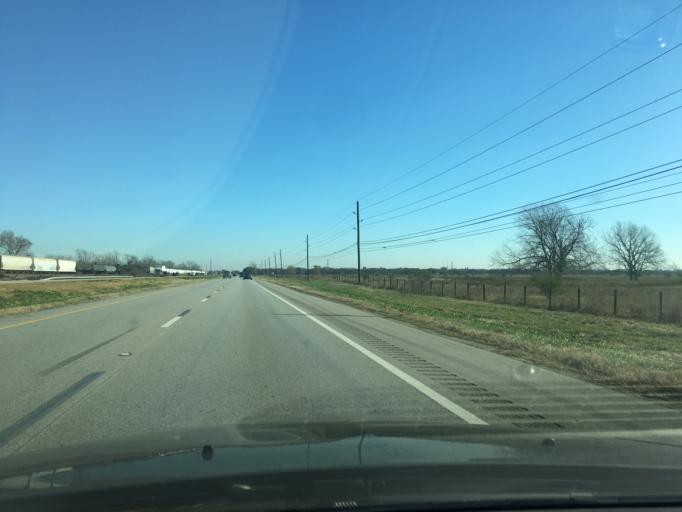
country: US
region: Texas
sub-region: Fort Bend County
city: New Territory
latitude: 29.5989
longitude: -95.7098
